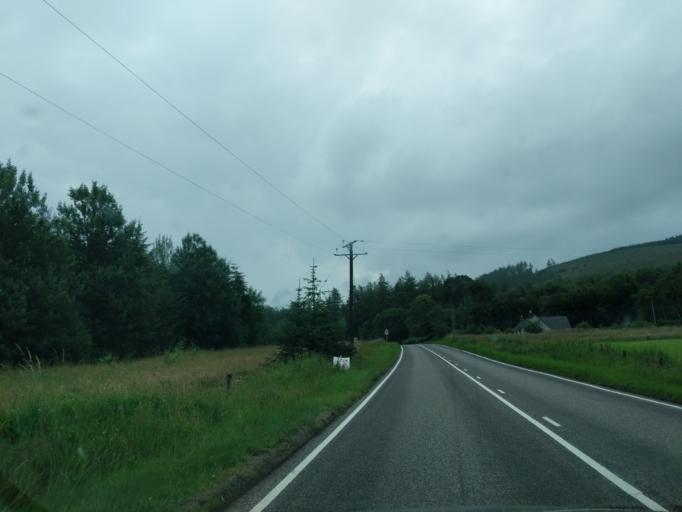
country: GB
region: Scotland
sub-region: Moray
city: Rothes
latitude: 57.4811
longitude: -3.1757
